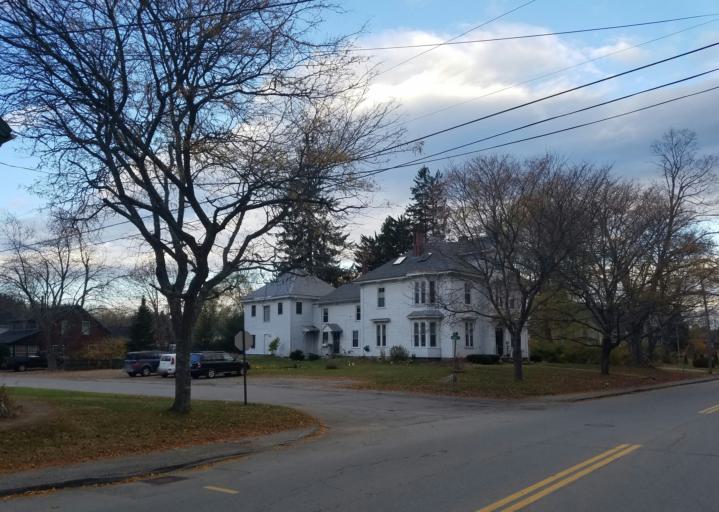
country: US
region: Maine
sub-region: Waldo County
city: Belfast
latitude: 44.4288
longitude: -69.0124
